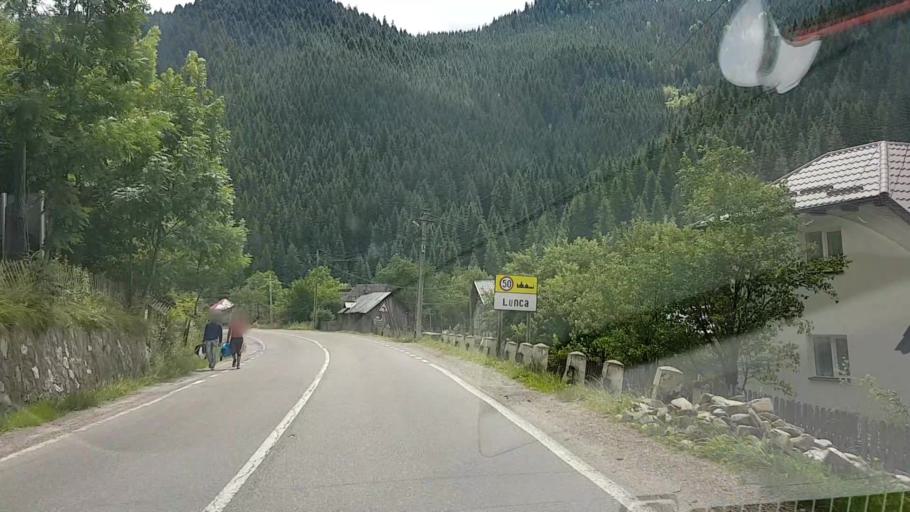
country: RO
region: Suceava
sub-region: Comuna Brosteni
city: Brosteni
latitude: 47.2186
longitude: 25.7377
